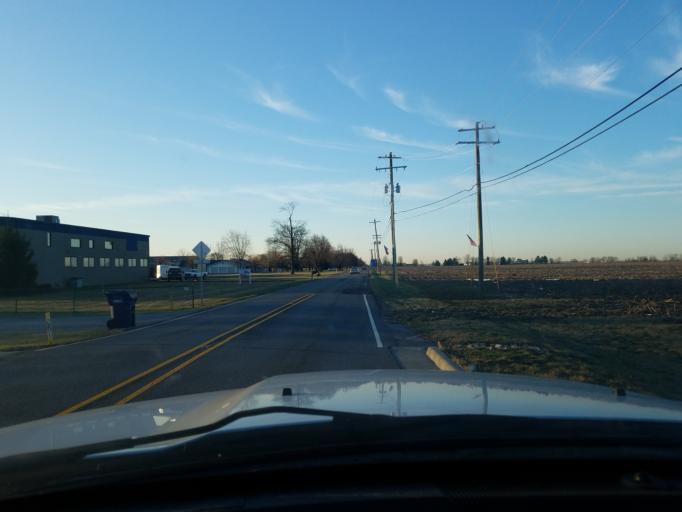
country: US
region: Indiana
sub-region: Johnson County
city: Whiteland
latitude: 39.5497
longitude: -86.0592
